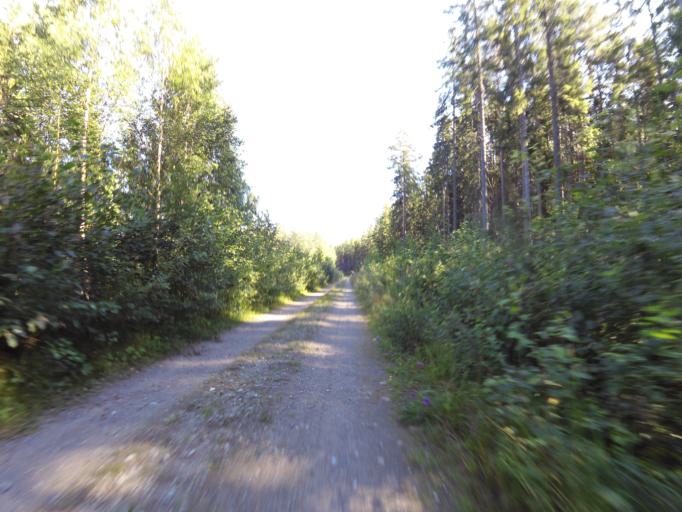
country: SE
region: Gaevleborg
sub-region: Hofors Kommun
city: Hofors
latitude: 60.5459
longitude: 16.4341
